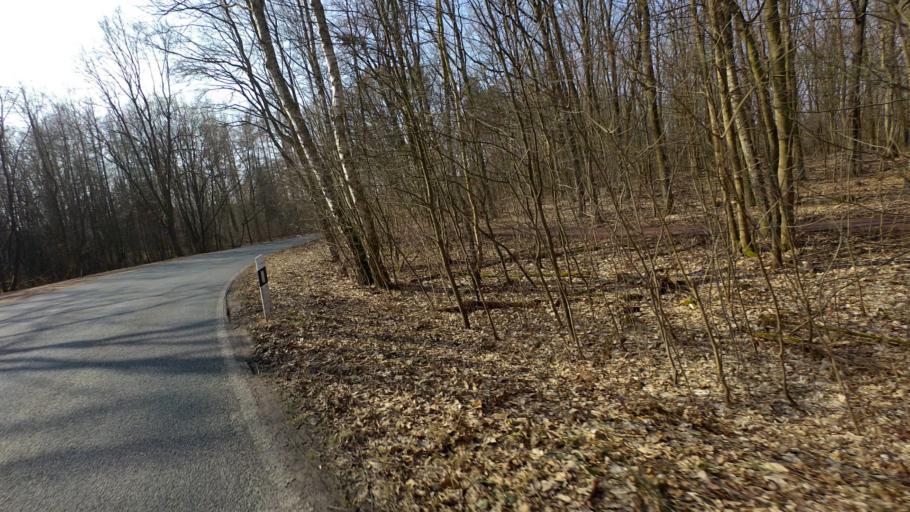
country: DE
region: Brandenburg
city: Werder
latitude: 52.3303
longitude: 12.9690
